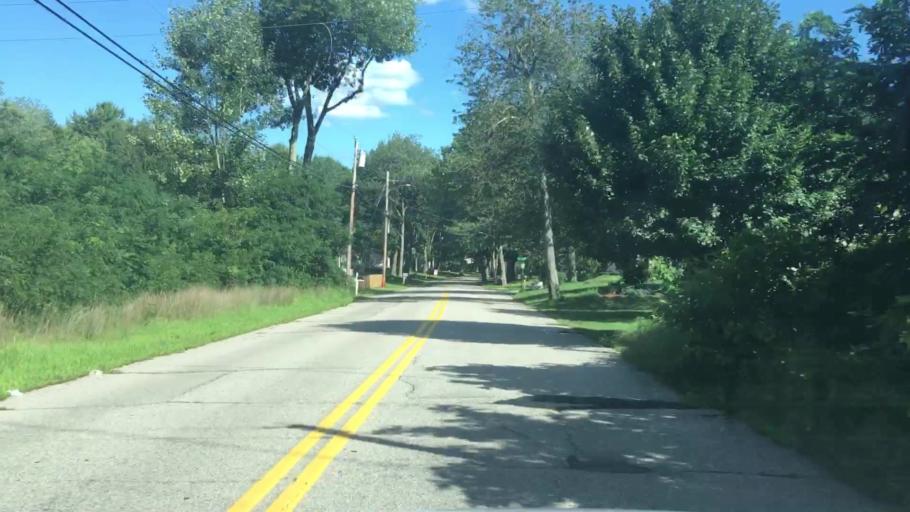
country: US
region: New Hampshire
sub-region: Strafford County
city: Dover
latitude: 43.1585
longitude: -70.8720
